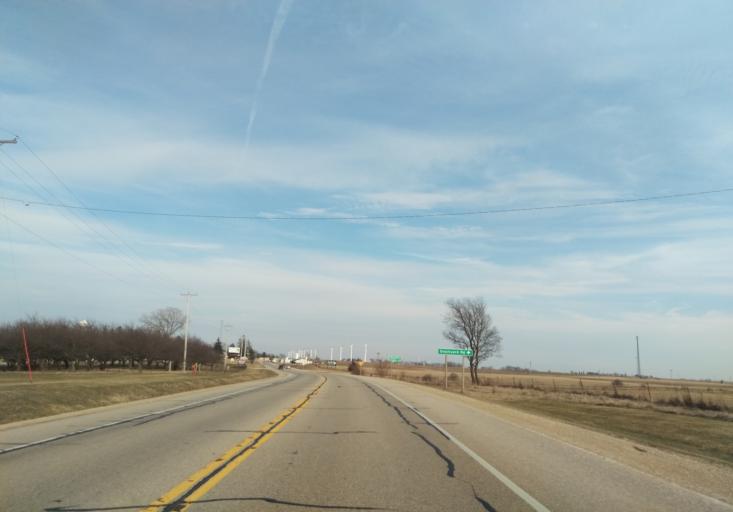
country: US
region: Wisconsin
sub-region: Grant County
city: Fennimore
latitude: 42.9662
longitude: -90.4416
